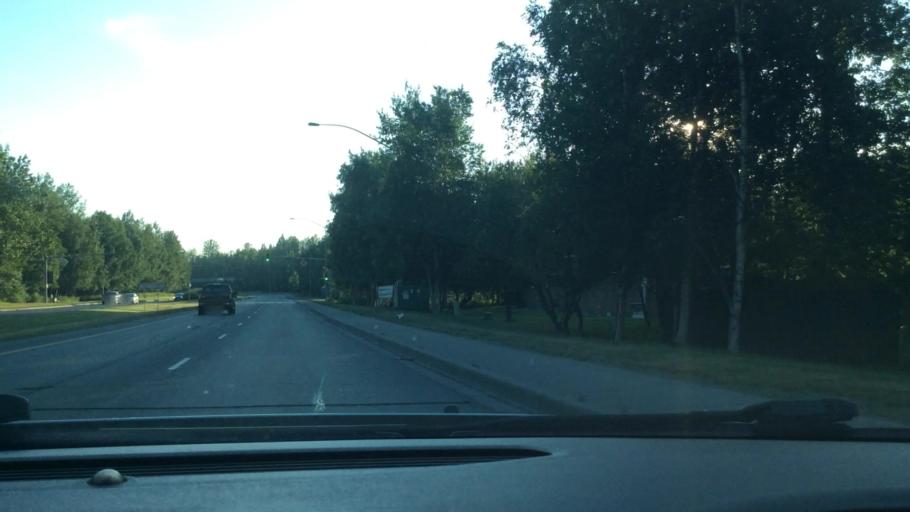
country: US
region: Alaska
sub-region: Anchorage Municipality
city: Anchorage
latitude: 61.1990
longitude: -149.8135
